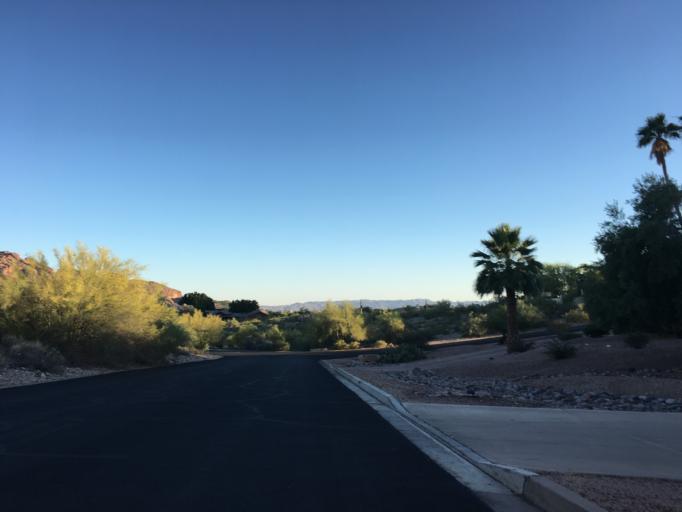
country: US
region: Arizona
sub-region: Maricopa County
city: Paradise Valley
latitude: 33.5395
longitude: -111.9805
